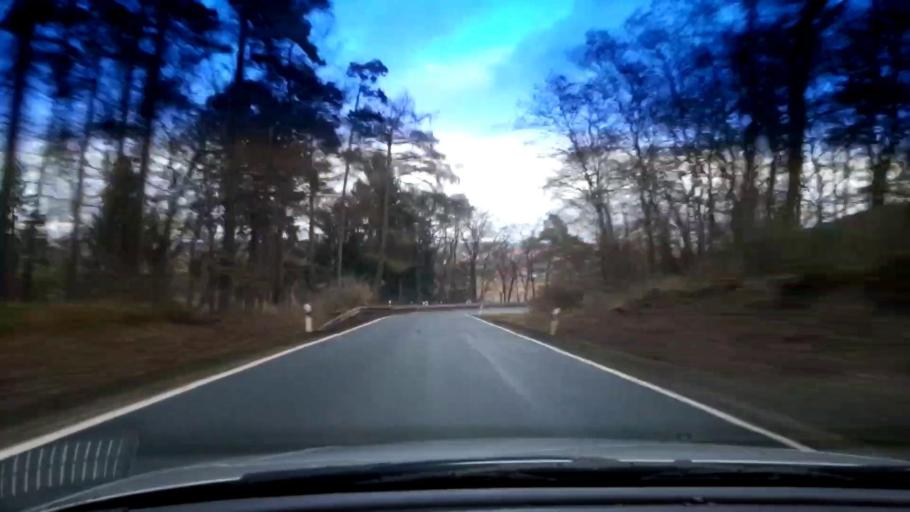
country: DE
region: Bavaria
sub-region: Upper Franconia
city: Walsdorf
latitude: 49.8700
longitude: 10.7703
